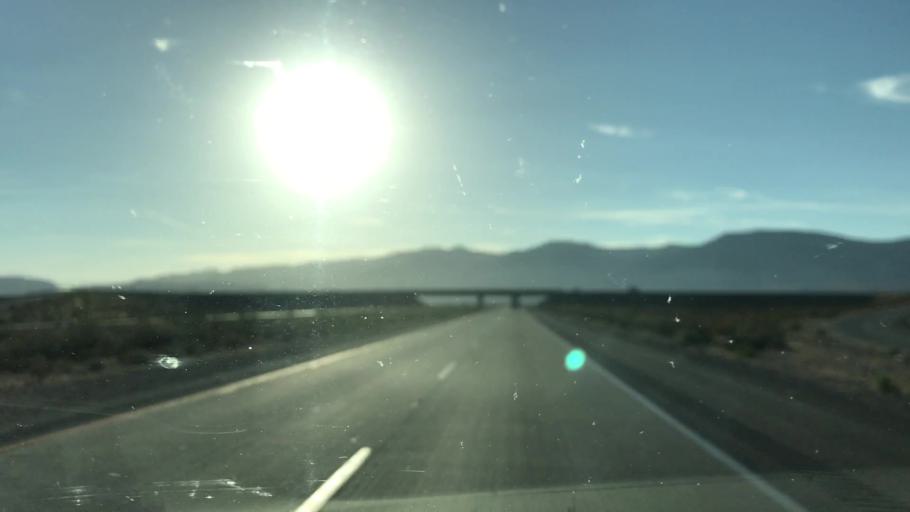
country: US
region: California
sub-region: Kern County
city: Mojave
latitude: 35.0966
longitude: -118.1390
